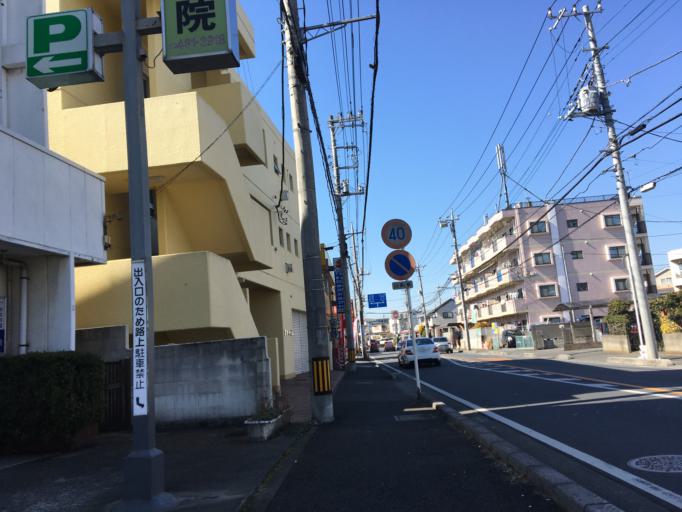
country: JP
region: Saitama
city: Shiki
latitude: 35.8180
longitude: 139.5623
